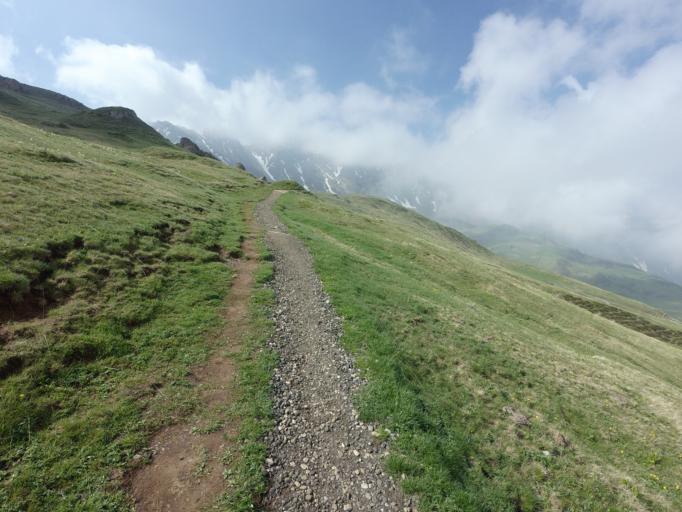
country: IT
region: Trentino-Alto Adige
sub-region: Bolzano
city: Ortisei
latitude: 46.5149
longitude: 11.6346
